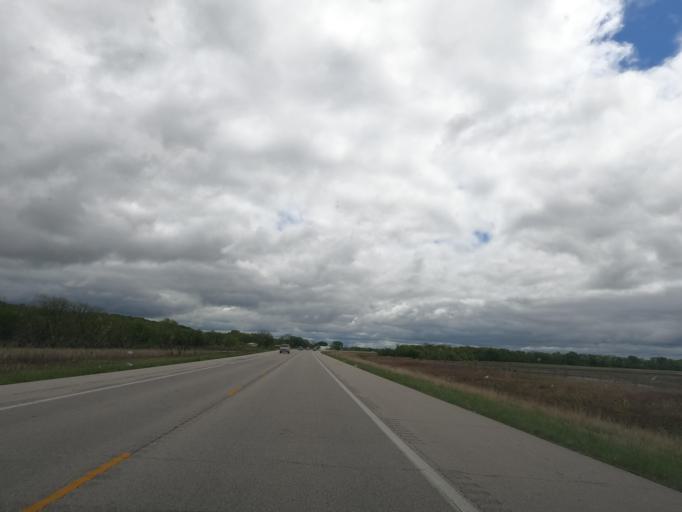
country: US
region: Kansas
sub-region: Wilson County
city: Neodesha
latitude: 37.4412
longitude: -95.7121
